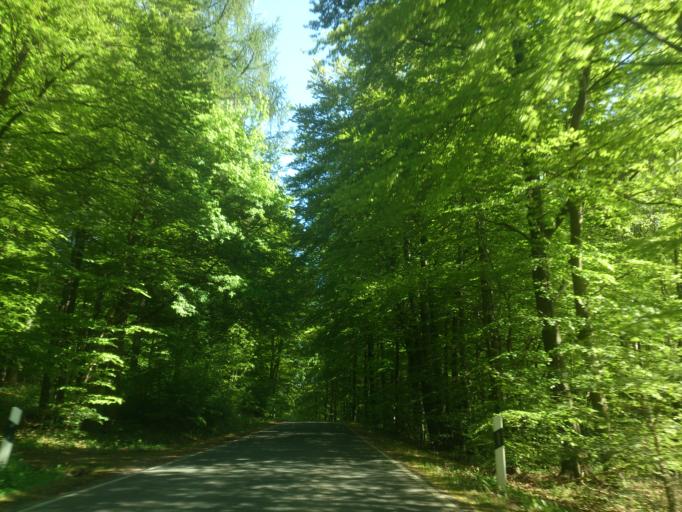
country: DE
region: North Rhine-Westphalia
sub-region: Regierungsbezirk Detmold
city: Willebadessen
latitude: 51.6570
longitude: 9.0328
